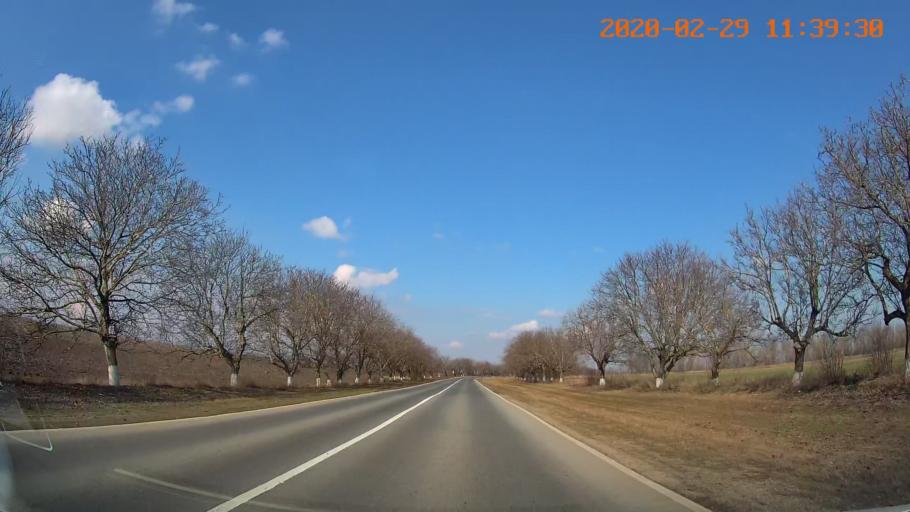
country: MD
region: Rezina
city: Saharna
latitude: 47.6410
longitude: 29.0247
